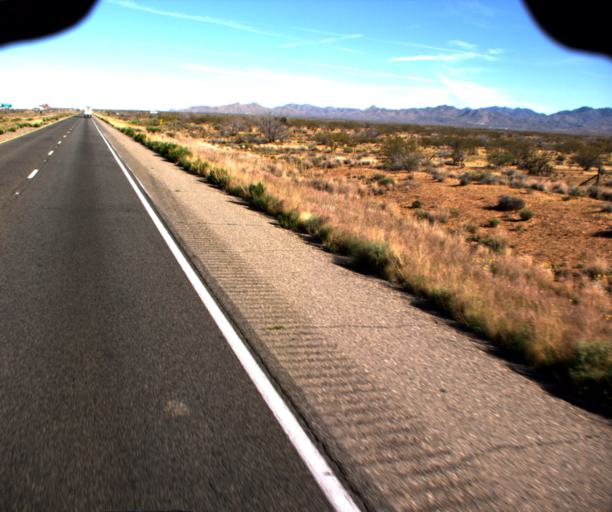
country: US
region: Arizona
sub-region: Mohave County
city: Golden Valley
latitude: 35.3271
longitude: -114.2086
